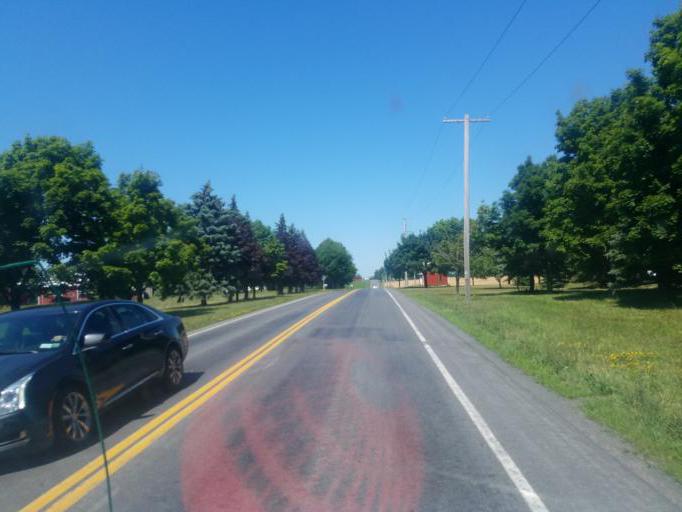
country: US
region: New York
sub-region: Ontario County
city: Geneva
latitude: 42.7681
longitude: -77.0118
